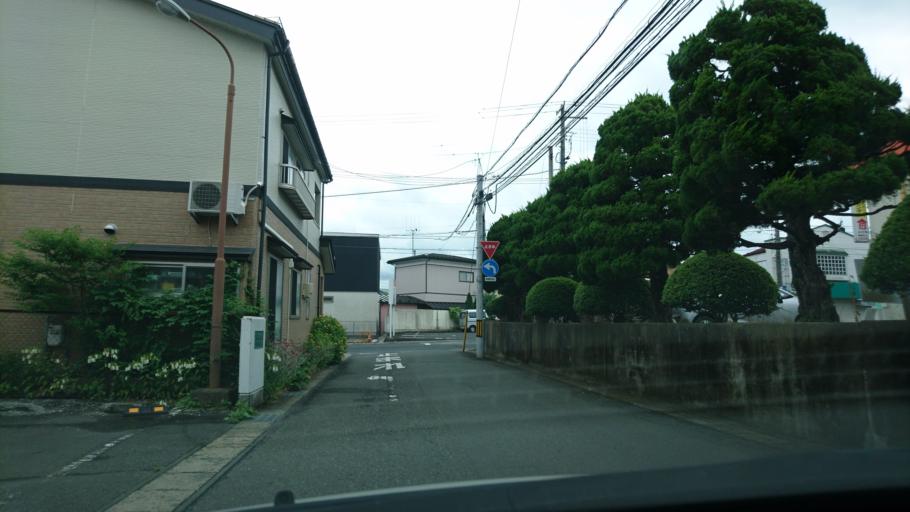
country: JP
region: Iwate
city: Ichinoseki
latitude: 38.9341
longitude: 141.1280
